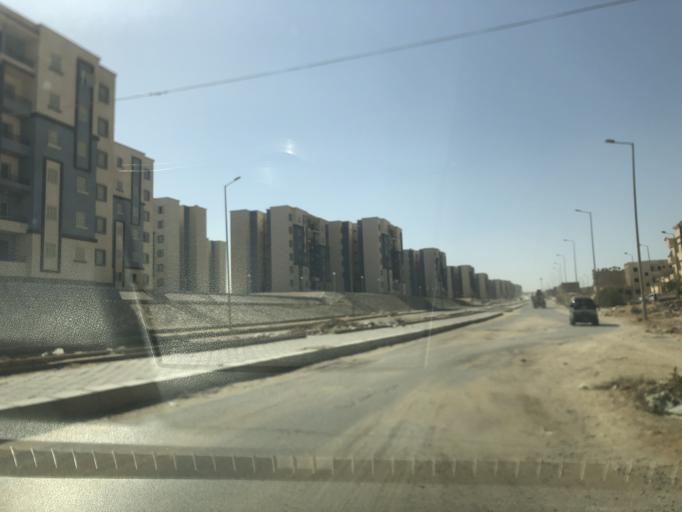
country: EG
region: Al Jizah
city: Madinat Sittah Uktubar
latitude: 29.9294
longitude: 30.9904
